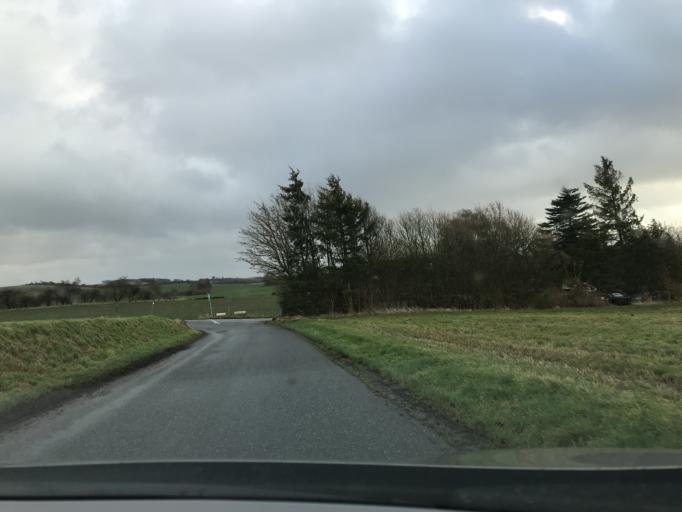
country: DK
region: South Denmark
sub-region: Assens Kommune
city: Arup
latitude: 55.3350
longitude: 9.9980
